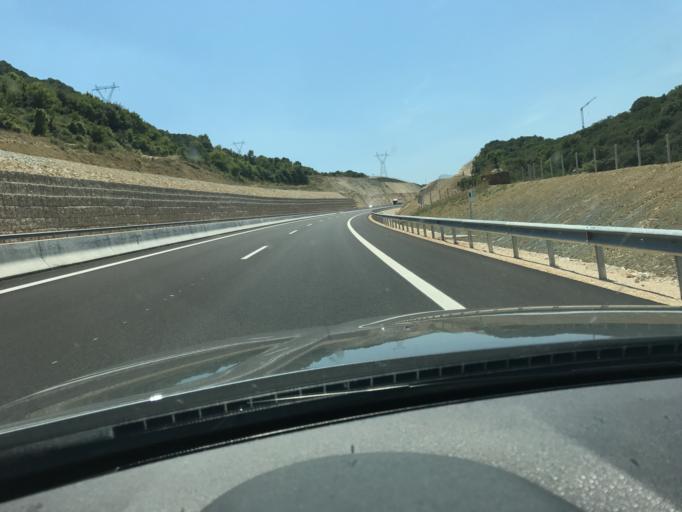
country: GR
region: Epirus
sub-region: Nomos Ioanninon
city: Agia Kyriaki
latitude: 39.5035
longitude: 20.8903
